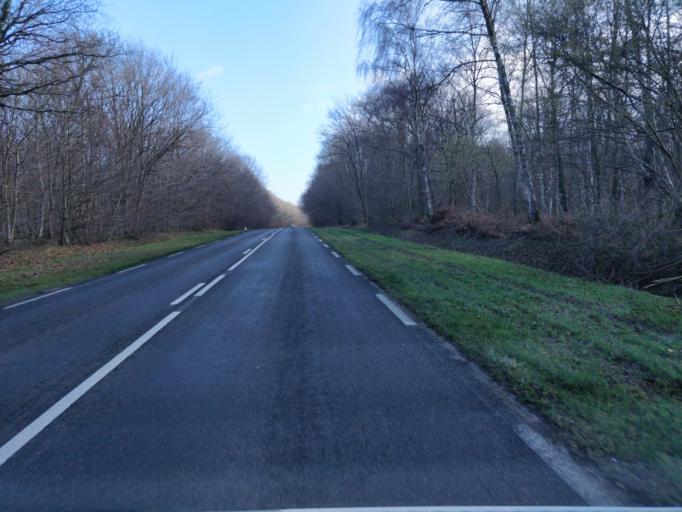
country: FR
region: Ile-de-France
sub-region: Departement de Seine-et-Marne
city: Souppes-sur-Loing
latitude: 48.2428
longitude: 2.7989
